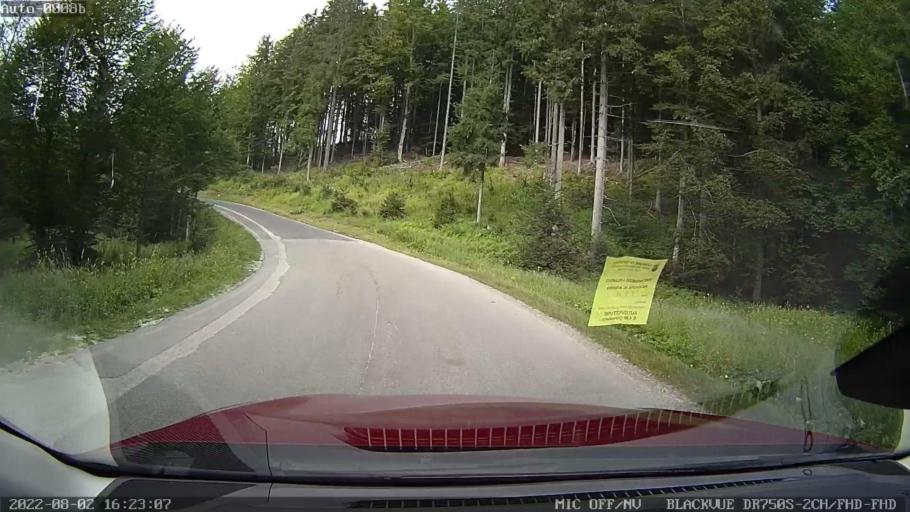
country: AT
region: Carinthia
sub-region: Politischer Bezirk Villach Land
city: Arnoldstein
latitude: 46.4761
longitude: 13.6721
